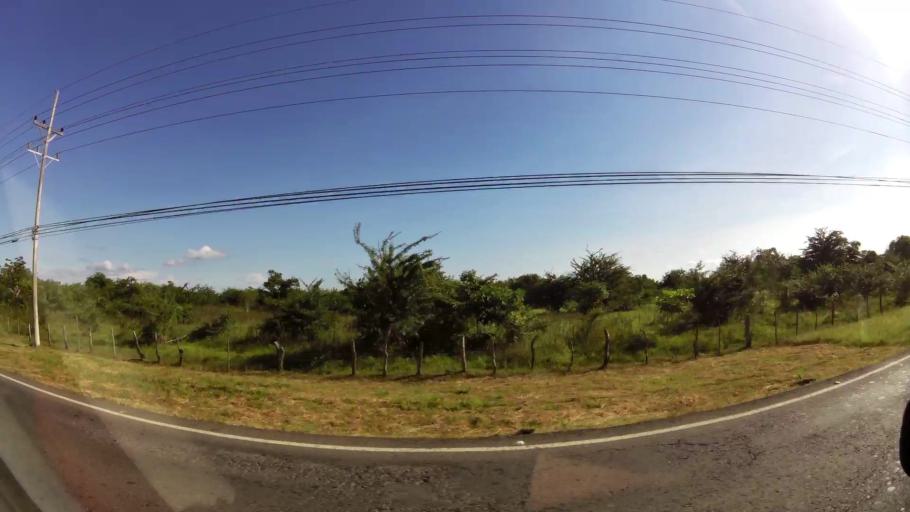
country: CR
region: Guanacaste
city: Liberia
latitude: 10.5903
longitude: -85.5448
